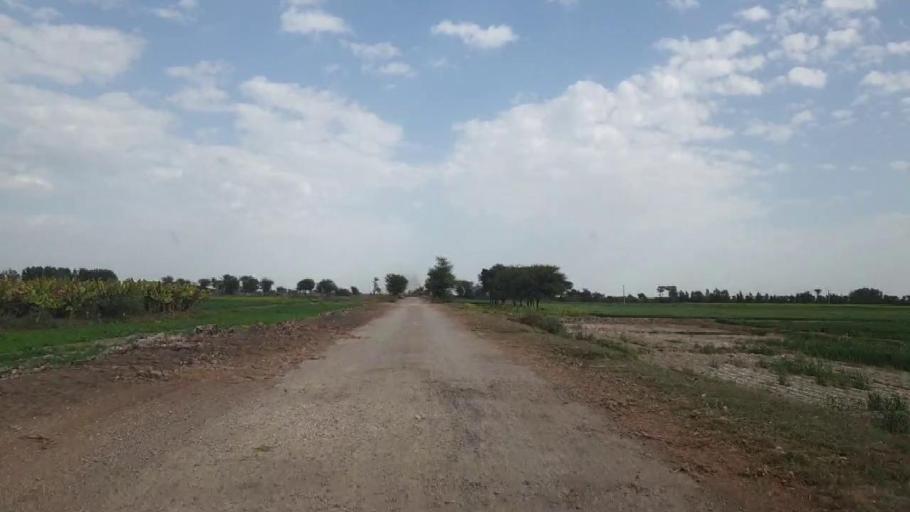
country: PK
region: Sindh
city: Shahdadpur
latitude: 25.9657
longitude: 68.4731
